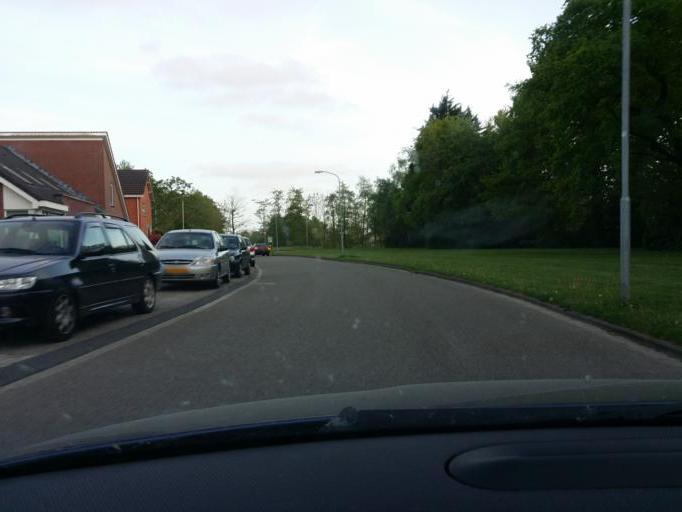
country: NL
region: Groningen
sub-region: Gemeente Grootegast
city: Grootegast
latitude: 53.2100
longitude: 6.2746
